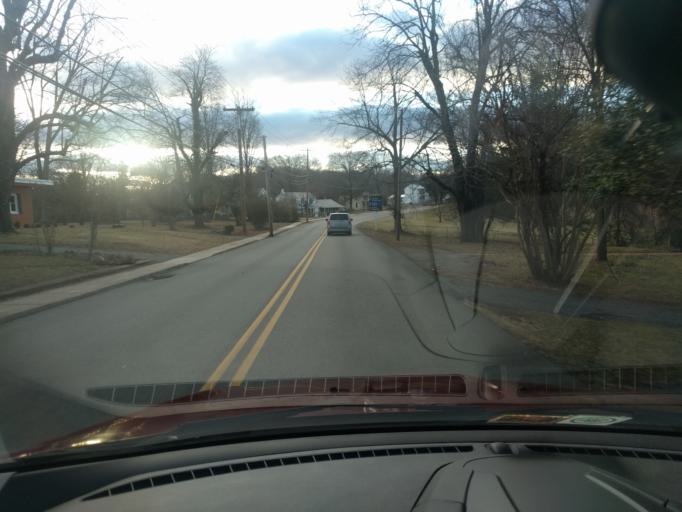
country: US
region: Virginia
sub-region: City of Bedford
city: Bedford
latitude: 37.3439
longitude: -79.5268
